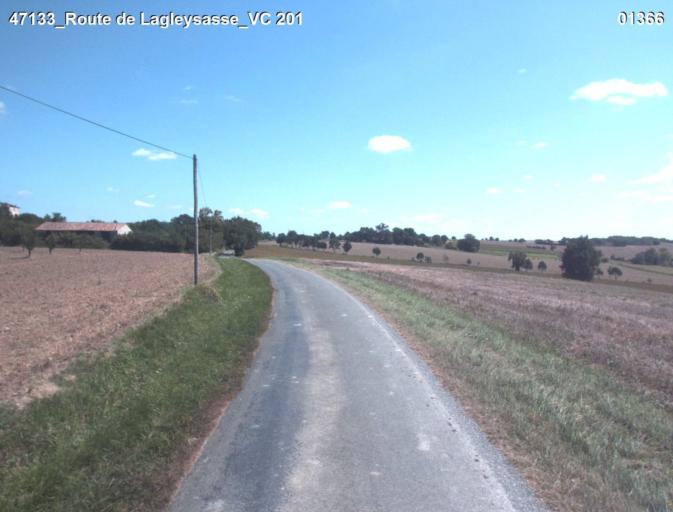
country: FR
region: Aquitaine
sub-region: Departement du Lot-et-Garonne
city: Laplume
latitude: 44.0590
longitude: 0.5431
